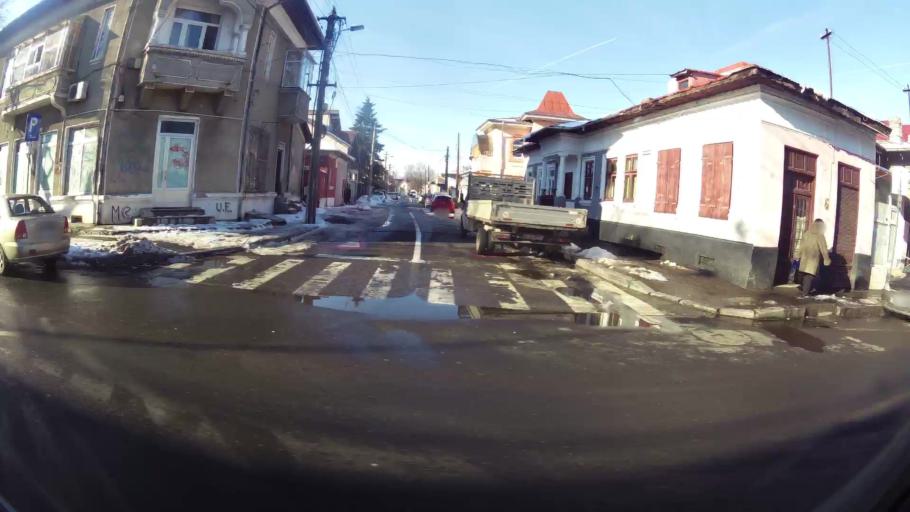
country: RO
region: Bucuresti
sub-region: Municipiul Bucuresti
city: Bucuresti
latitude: 44.4023
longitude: 26.0921
